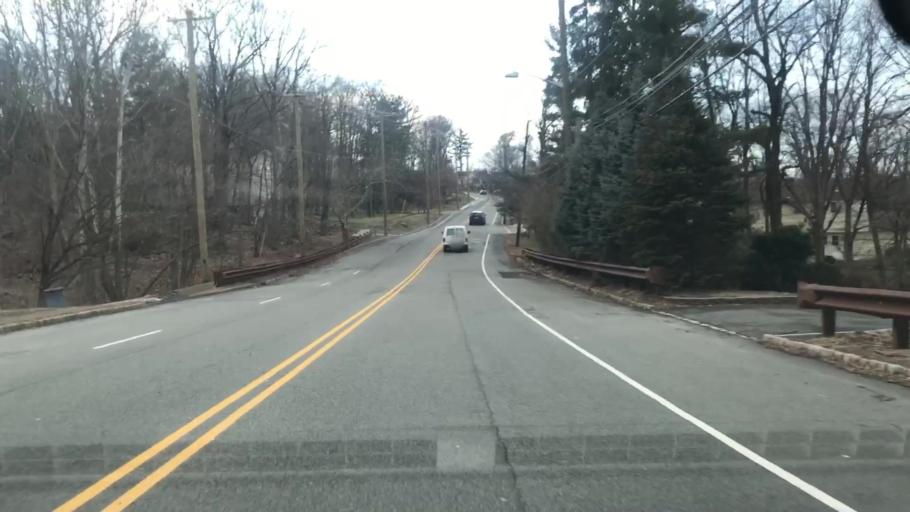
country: US
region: New Jersey
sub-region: Essex County
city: Livingston
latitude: 40.7789
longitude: -74.3002
